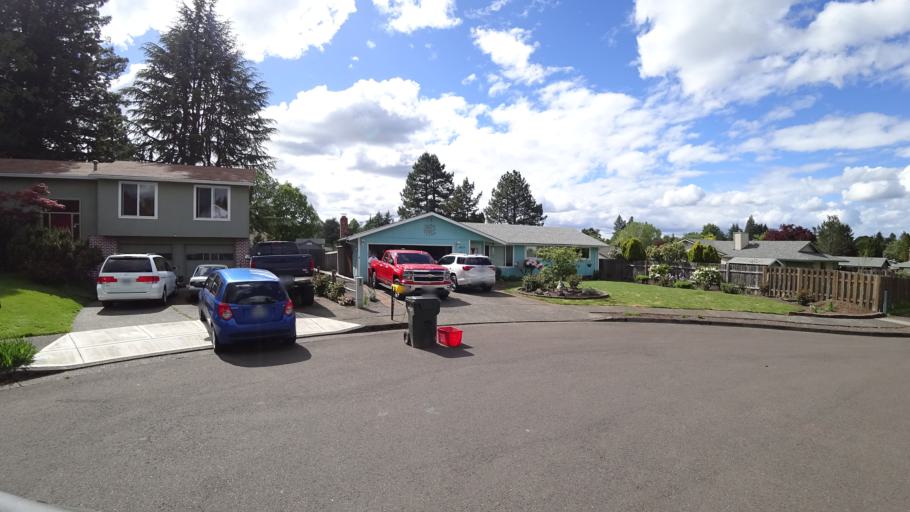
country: US
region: Oregon
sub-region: Washington County
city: Beaverton
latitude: 45.4799
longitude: -122.8199
